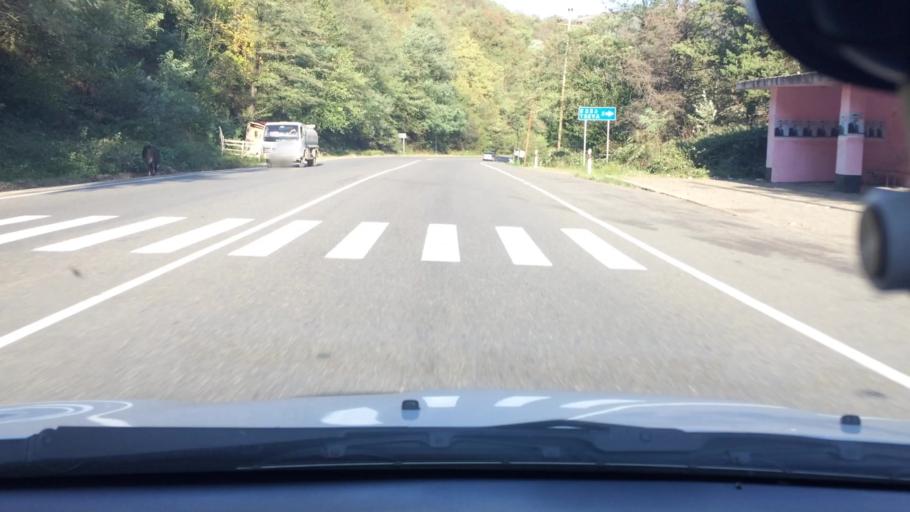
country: GE
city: Shorapani
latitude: 42.0917
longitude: 43.1311
